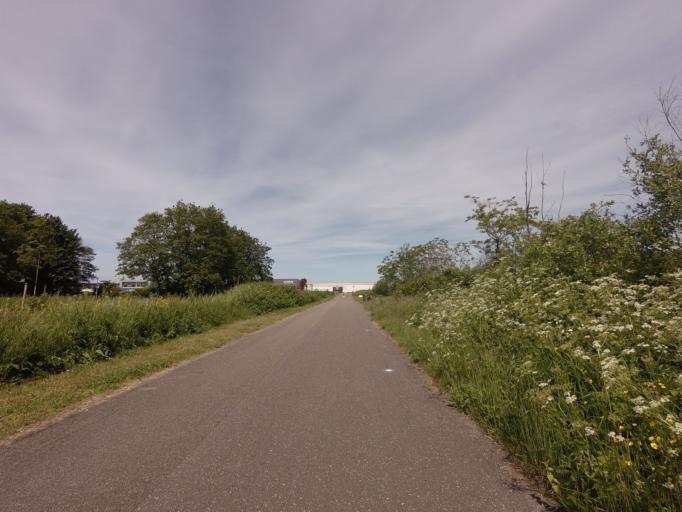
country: NL
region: North Holland
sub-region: Gemeente Zaanstad
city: Zaandam
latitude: 52.3884
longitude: 4.7774
